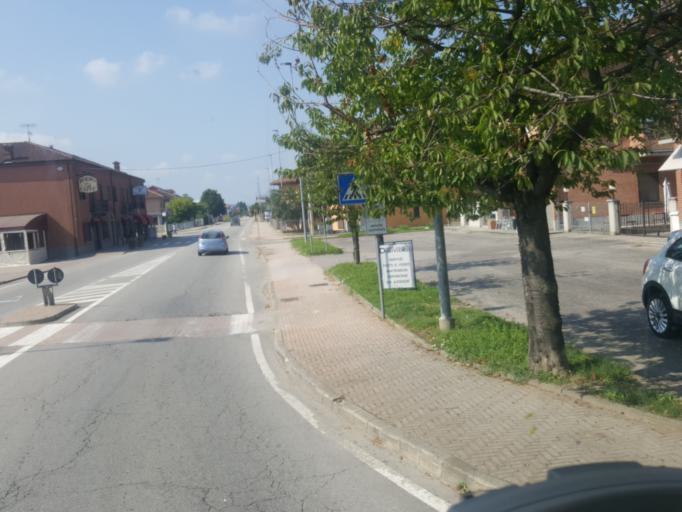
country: IT
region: Piedmont
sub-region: Provincia di Cuneo
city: Vaccheria
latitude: 44.7289
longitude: 8.0447
